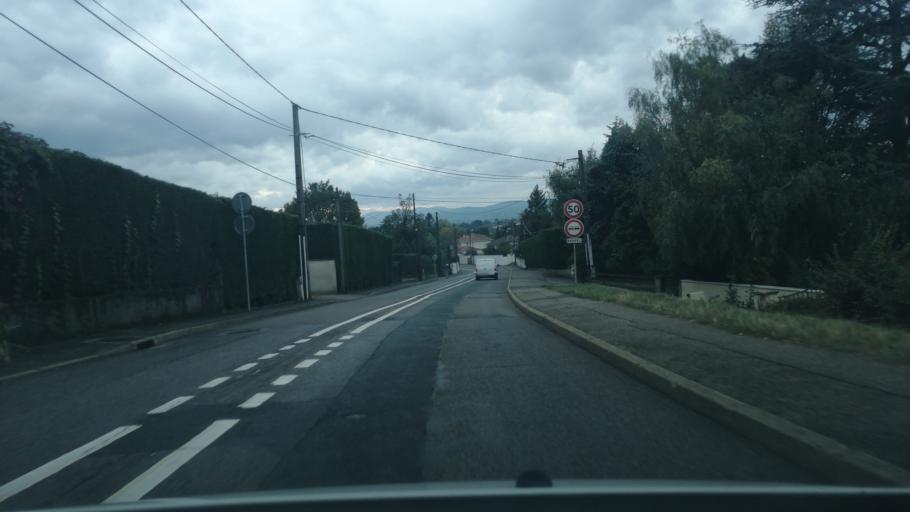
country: FR
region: Rhone-Alpes
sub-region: Departement du Rhone
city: Limonest
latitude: 45.8317
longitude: 4.7706
